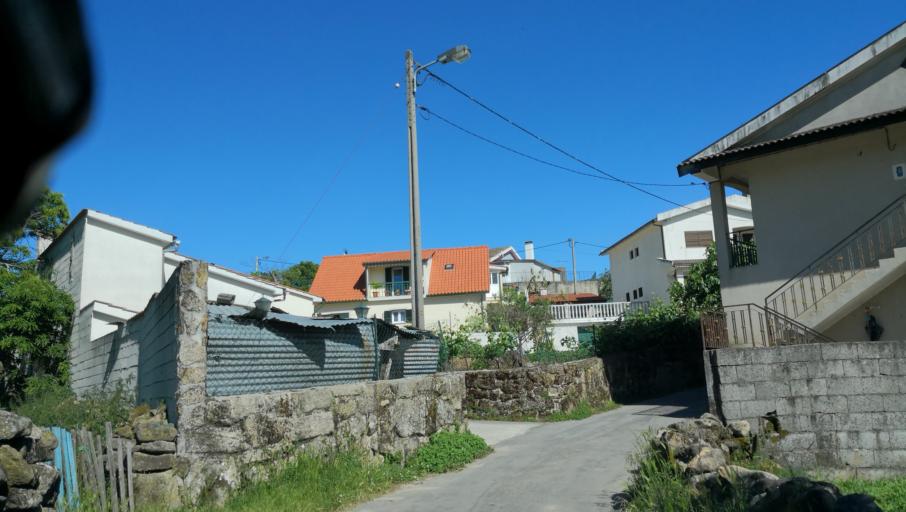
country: PT
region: Vila Real
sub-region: Vila Real
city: Vila Real
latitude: 41.2996
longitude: -7.6597
